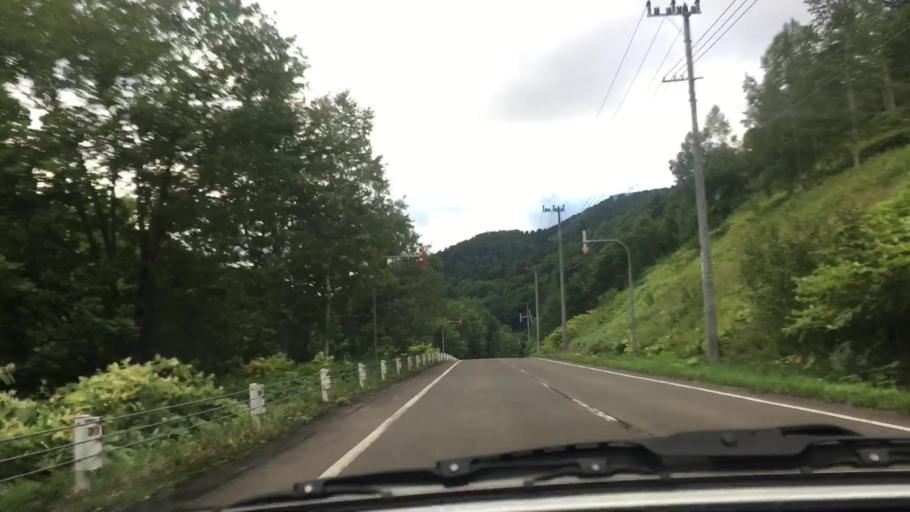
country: JP
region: Hokkaido
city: Shimo-furano
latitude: 43.0457
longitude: 142.5165
